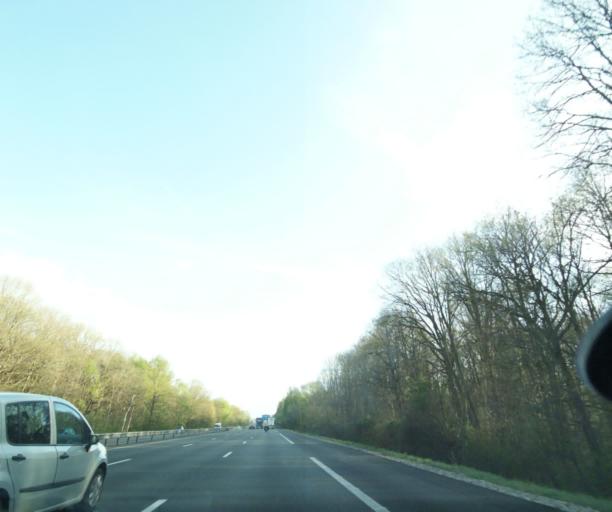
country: FR
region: Ile-de-France
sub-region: Departement de l'Essonne
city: Soisy-sur-Ecole
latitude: 48.4939
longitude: 2.5127
